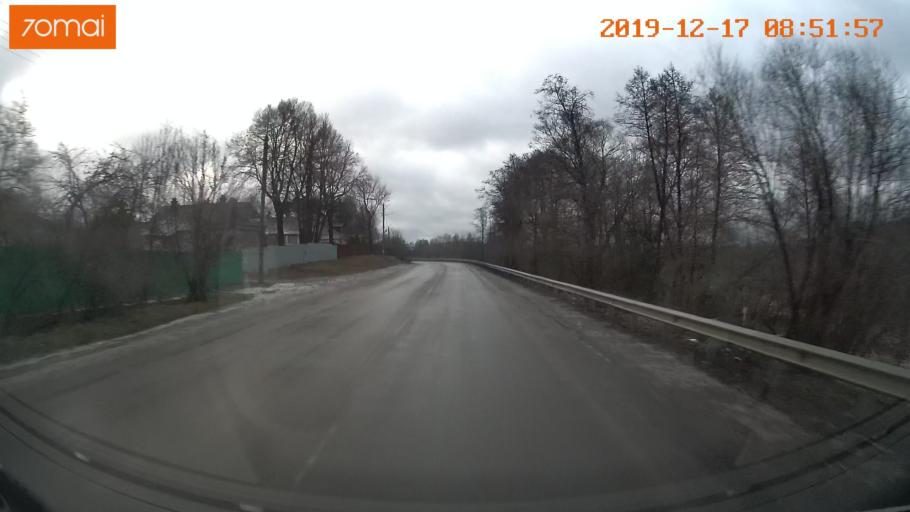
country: RU
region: Vladimir
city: Kosterevo
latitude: 55.9531
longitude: 39.6330
